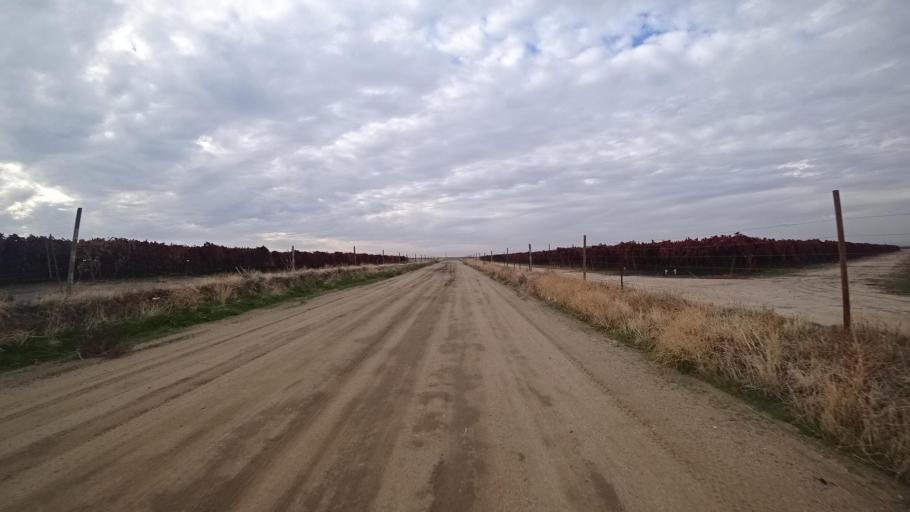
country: US
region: California
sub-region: Kern County
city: Arvin
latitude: 35.1435
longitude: -118.8120
